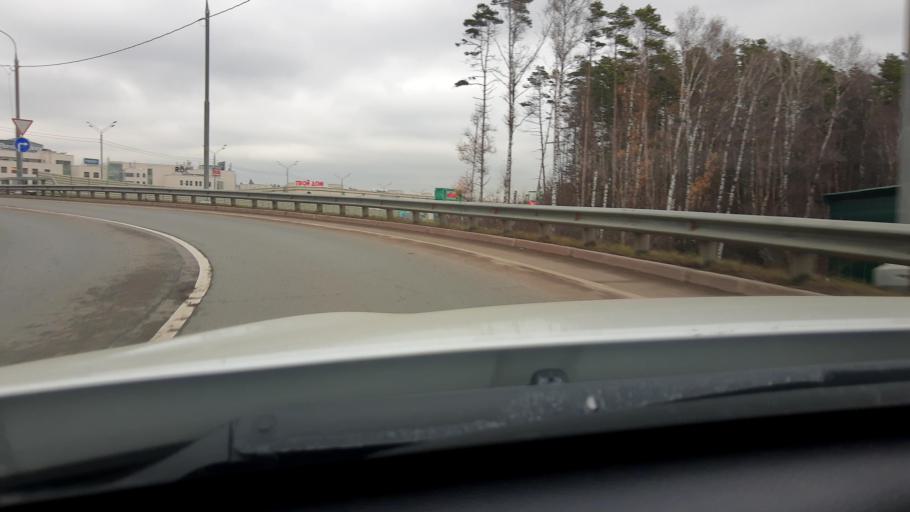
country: RU
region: Moskovskaya
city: Opalikha
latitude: 55.7821
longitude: 37.2424
